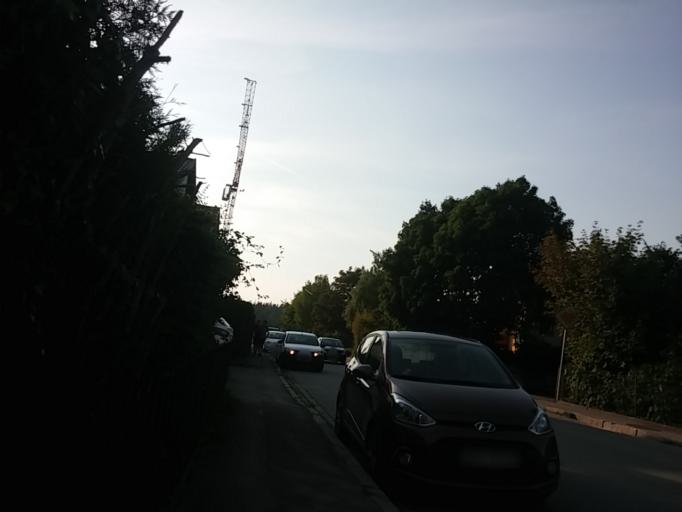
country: DE
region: Bavaria
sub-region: Upper Bavaria
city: Vaterstetten
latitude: 48.1136
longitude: 11.7712
